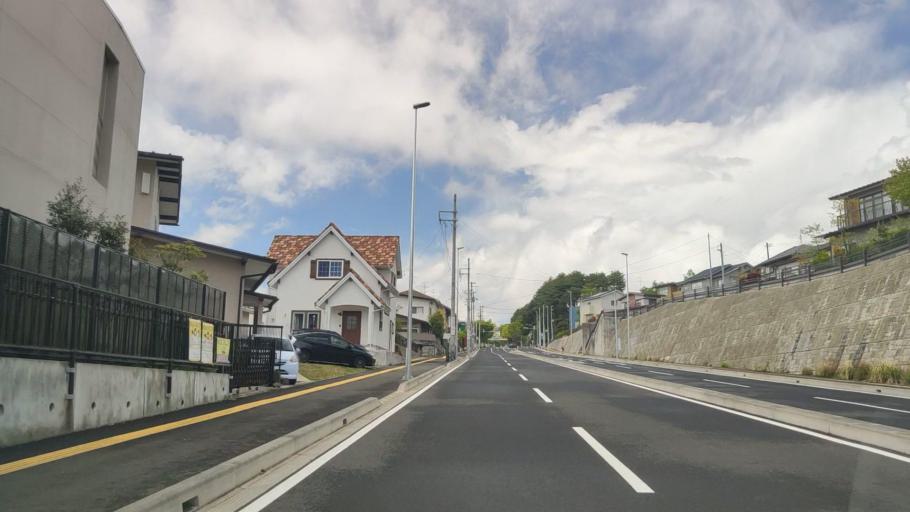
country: JP
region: Miyagi
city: Sendai
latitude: 38.2362
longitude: 140.8512
